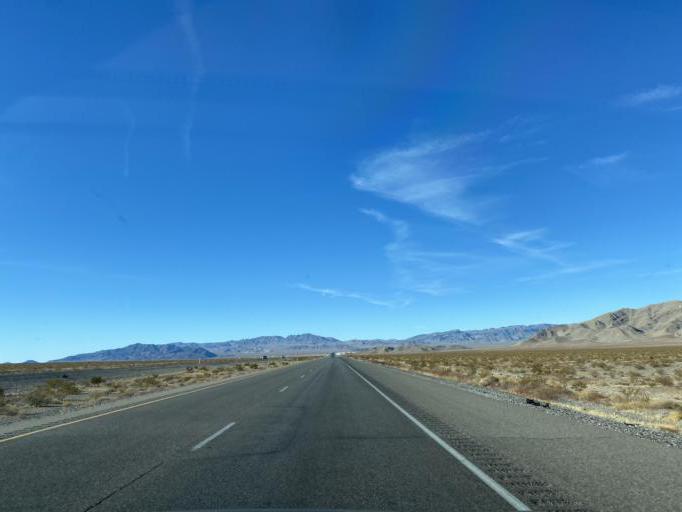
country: US
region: Nevada
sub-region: Nye County
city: Pahrump
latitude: 36.5648
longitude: -115.6206
